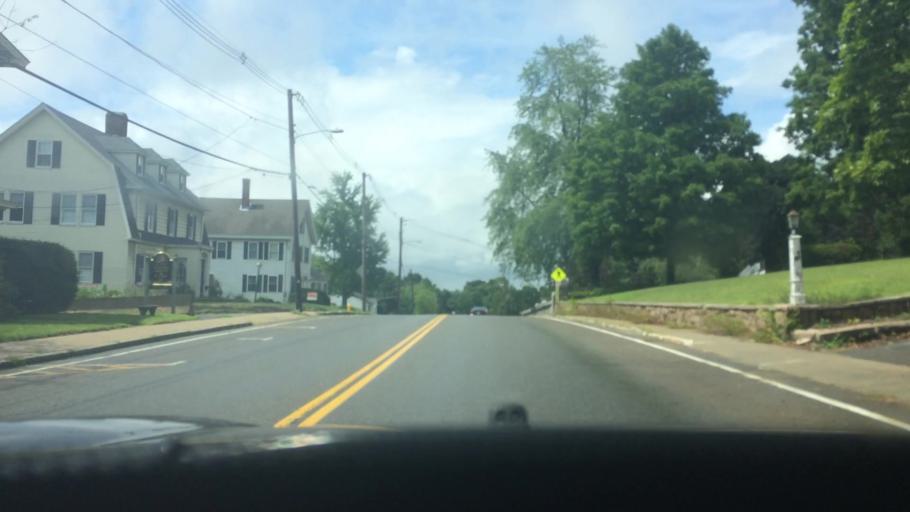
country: US
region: Massachusetts
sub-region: Worcester County
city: Gardner
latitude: 42.5793
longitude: -71.9878
